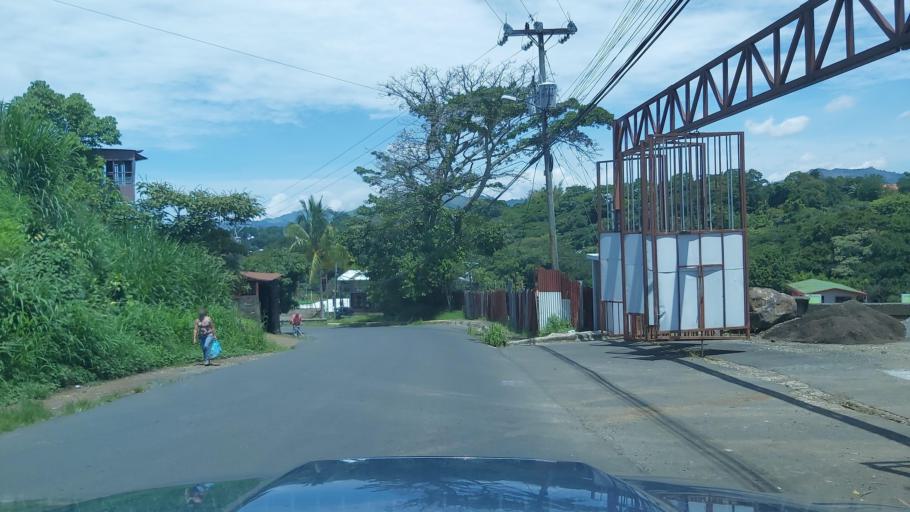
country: CR
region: Alajuela
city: San Juan
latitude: 10.0878
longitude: -84.3431
